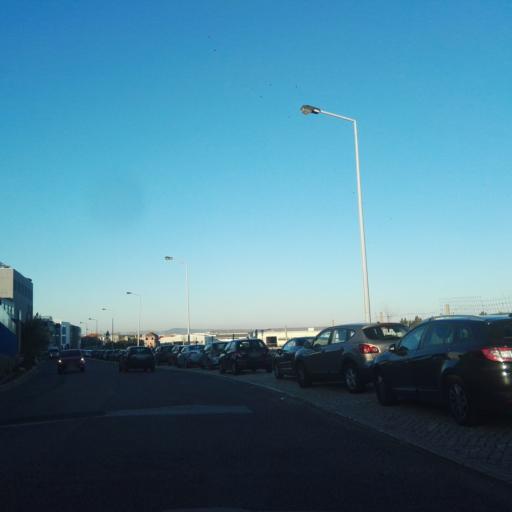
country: PT
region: Lisbon
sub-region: Loures
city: Camarate
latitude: 38.7844
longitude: -9.1296
